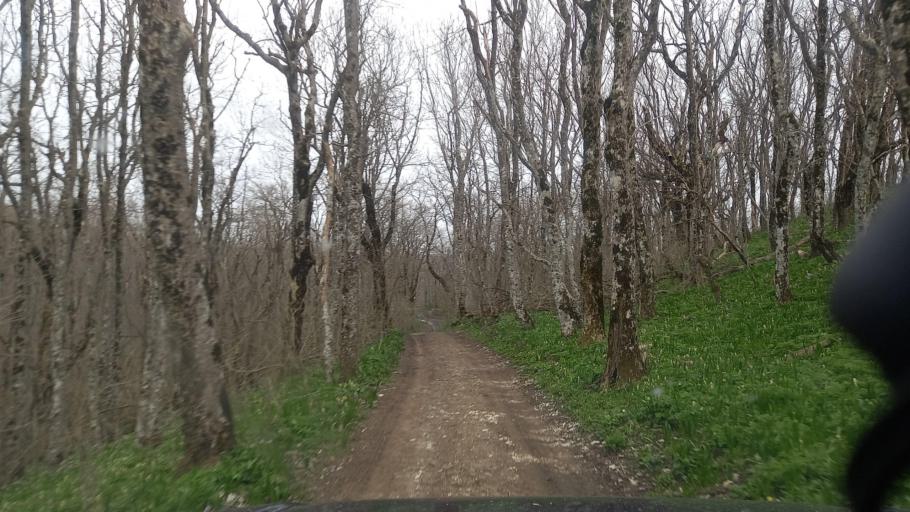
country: RU
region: Krasnodarskiy
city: Gelendzhik
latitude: 44.6141
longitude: 38.2064
